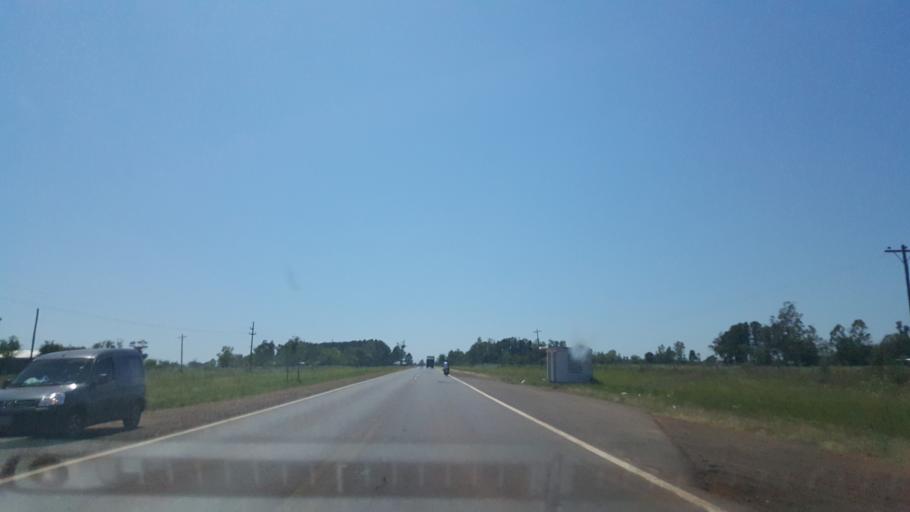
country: AR
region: Corrientes
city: Santo Tome
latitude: -28.5417
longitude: -56.0963
